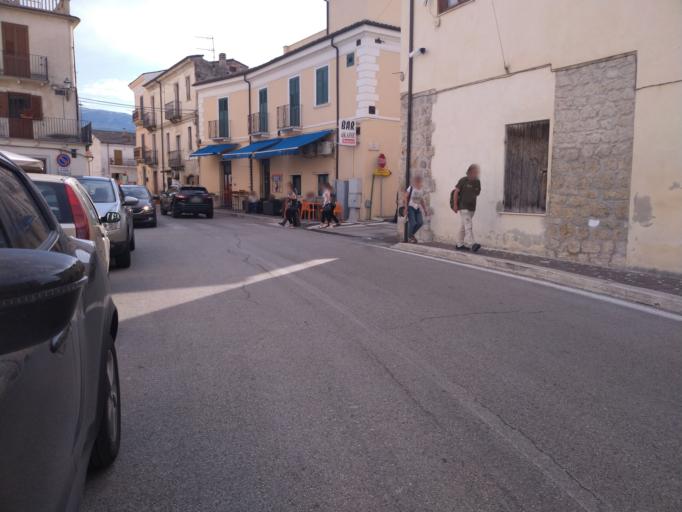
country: IT
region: Abruzzo
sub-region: Provincia dell' Aquila
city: Castelvecchio Subequo
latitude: 42.1307
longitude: 13.7308
